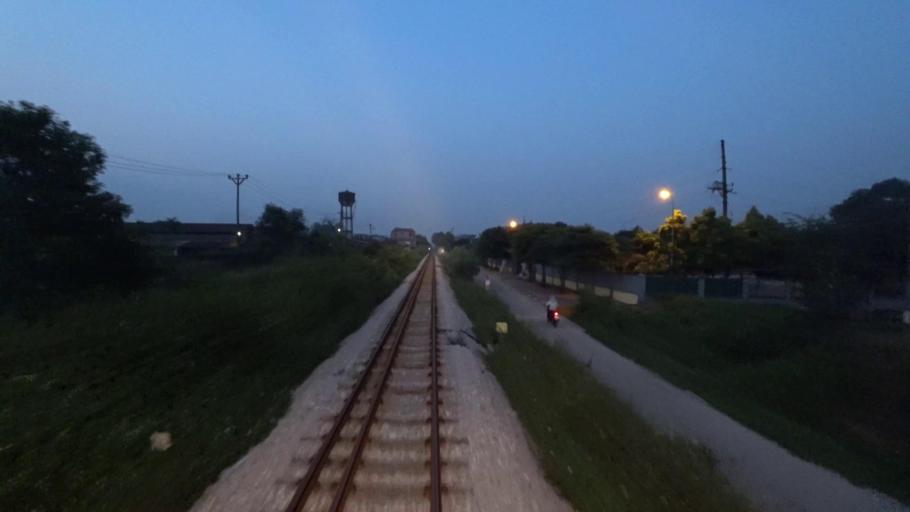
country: VN
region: Ha Noi
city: Soc Son
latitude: 21.2567
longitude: 105.8619
